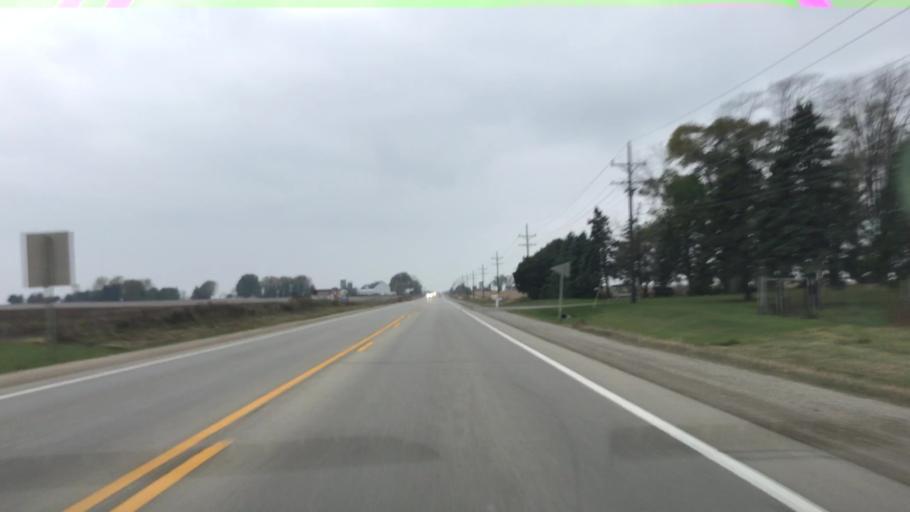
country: US
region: Wisconsin
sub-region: Outagamie County
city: Seymour
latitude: 44.5004
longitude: -88.2988
